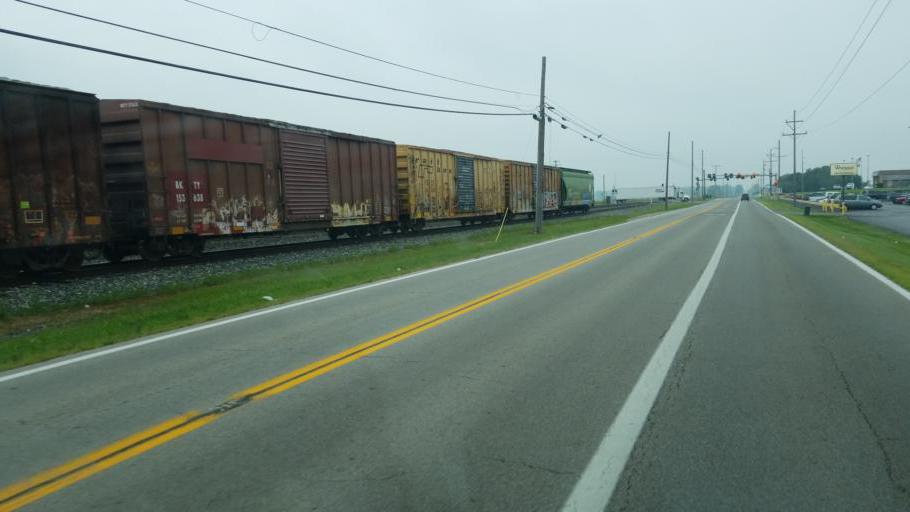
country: US
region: Ohio
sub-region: Marion County
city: Marion
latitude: 40.5861
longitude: -83.1621
